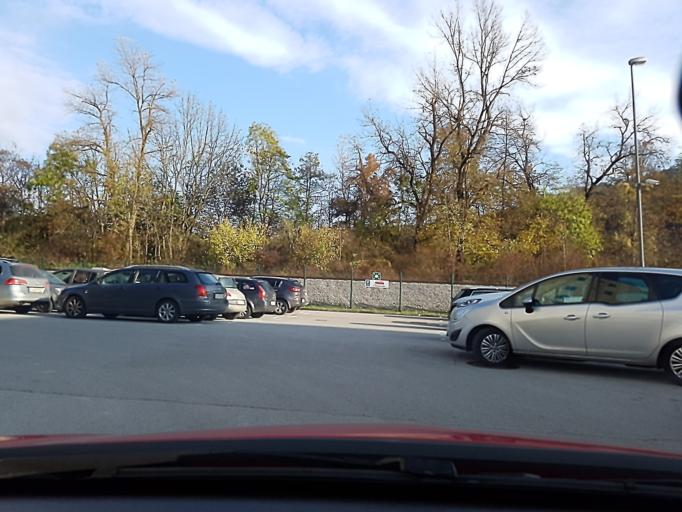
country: SI
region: Trzin
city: Trzin
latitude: 46.0946
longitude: 14.5583
